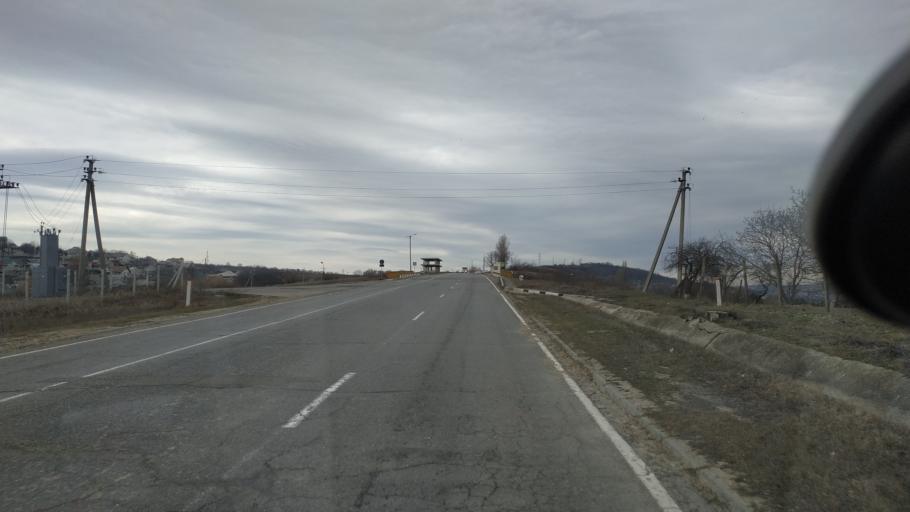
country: MD
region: Chisinau
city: Vadul lui Voda
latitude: 47.0846
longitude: 29.0782
